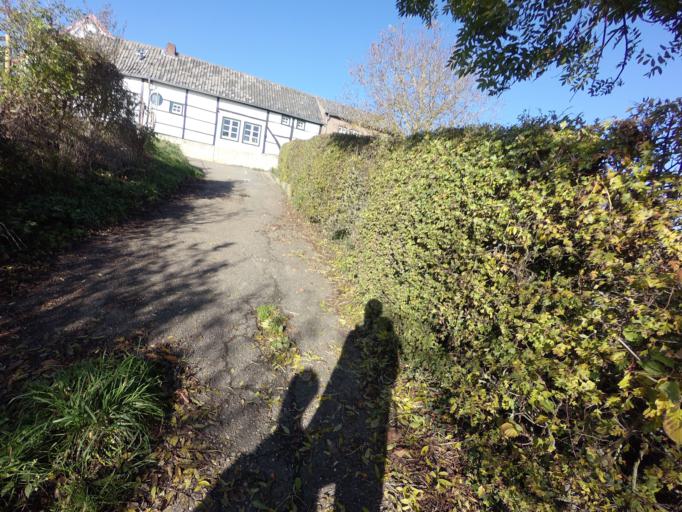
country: NL
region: Limburg
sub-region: Gemeente Voerendaal
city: Ubachsberg
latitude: 50.8370
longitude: 5.9329
